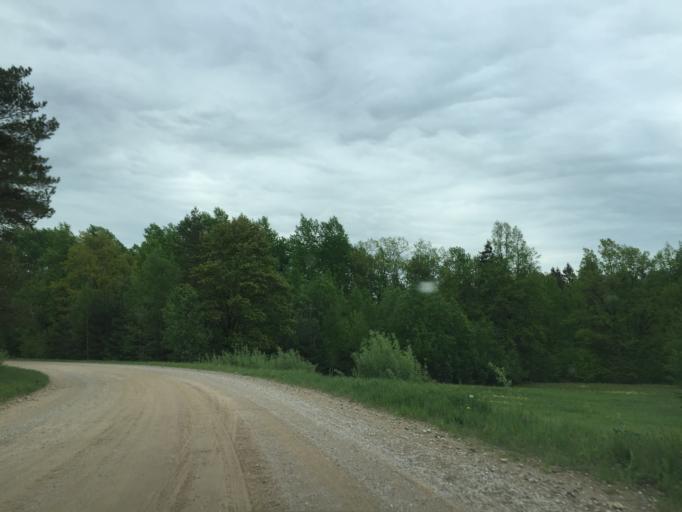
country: LV
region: Lielvarde
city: Lielvarde
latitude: 56.8045
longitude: 24.8497
